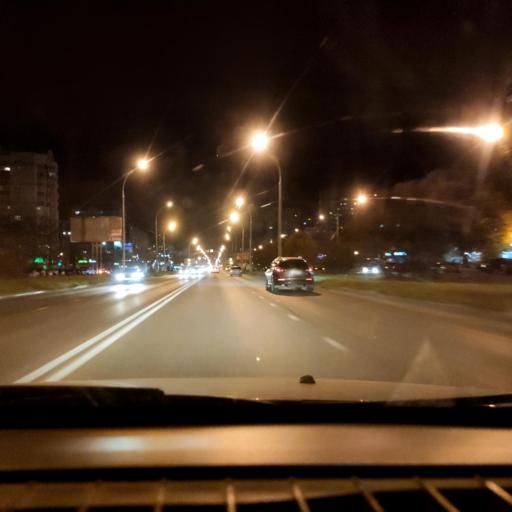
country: RU
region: Samara
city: Tol'yatti
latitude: 53.5420
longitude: 49.3345
